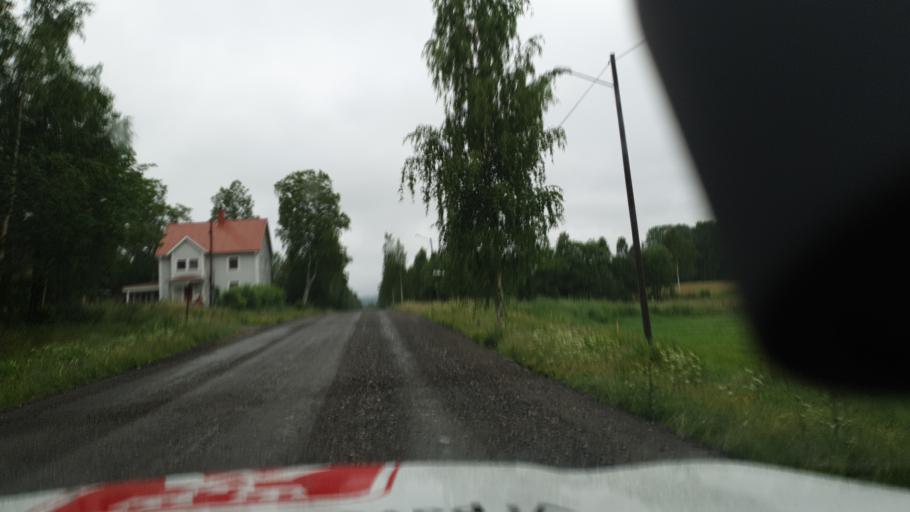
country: SE
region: Vaesterbotten
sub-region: Vannas Kommun
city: Vaennaes
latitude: 63.7485
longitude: 19.6443
